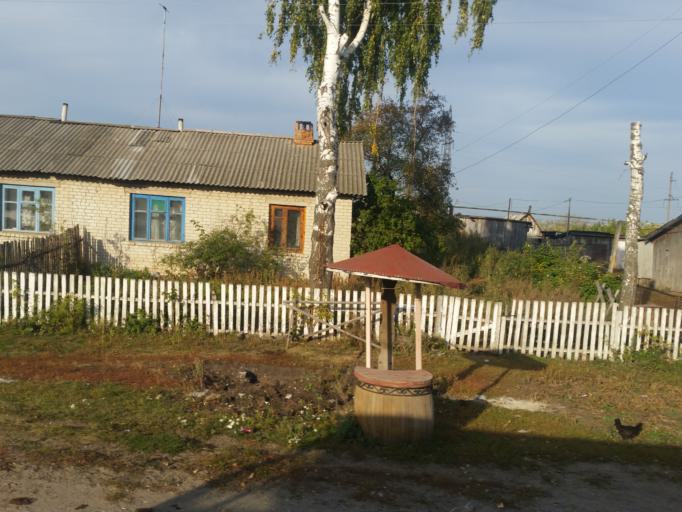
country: RU
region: Ulyanovsk
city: Mullovka
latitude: 54.2661
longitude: 49.1690
